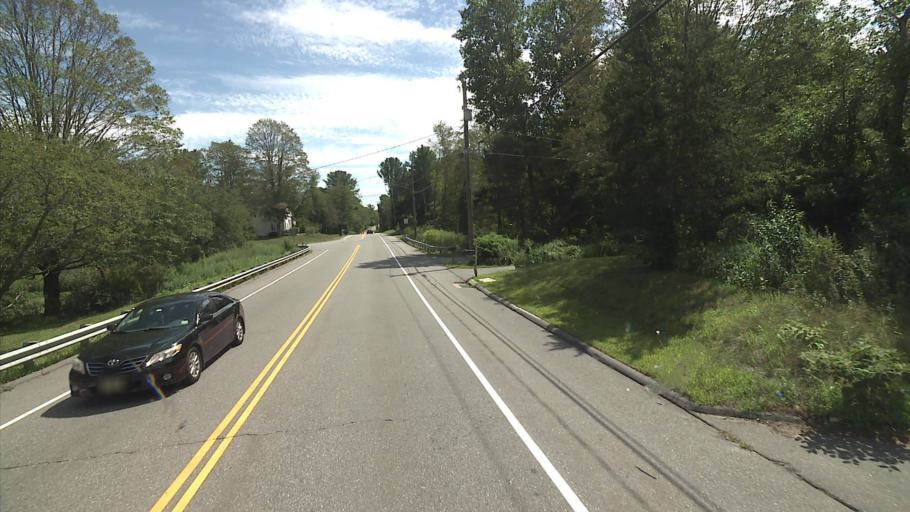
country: US
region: Connecticut
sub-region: Tolland County
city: Mansfield City
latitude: 41.7709
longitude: -72.2036
